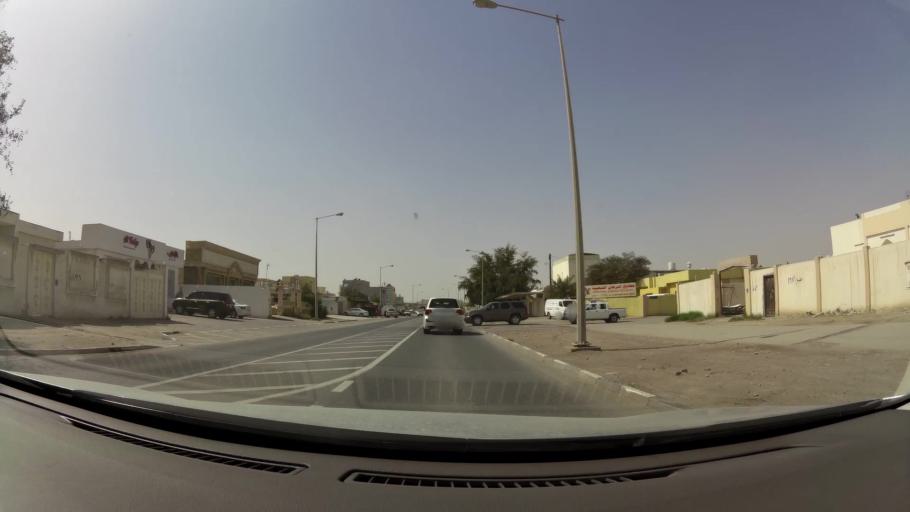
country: QA
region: Baladiyat Umm Salal
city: Umm Salal Muhammad
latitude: 25.3998
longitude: 51.4229
